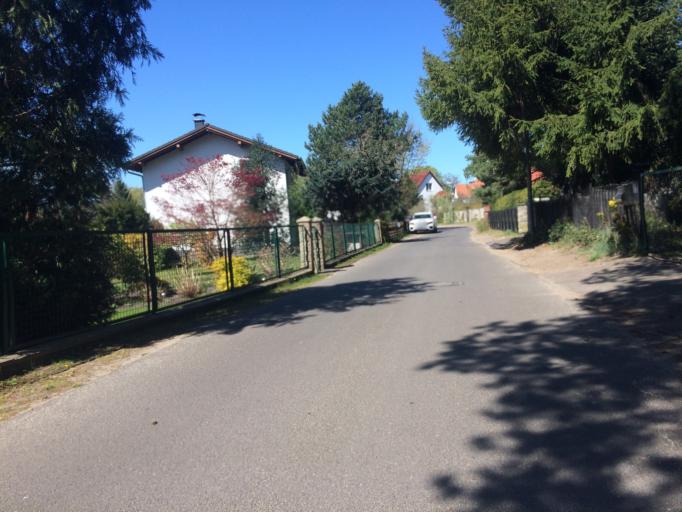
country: DE
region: Berlin
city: Rahnsdorf
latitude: 52.4346
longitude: 13.6996
